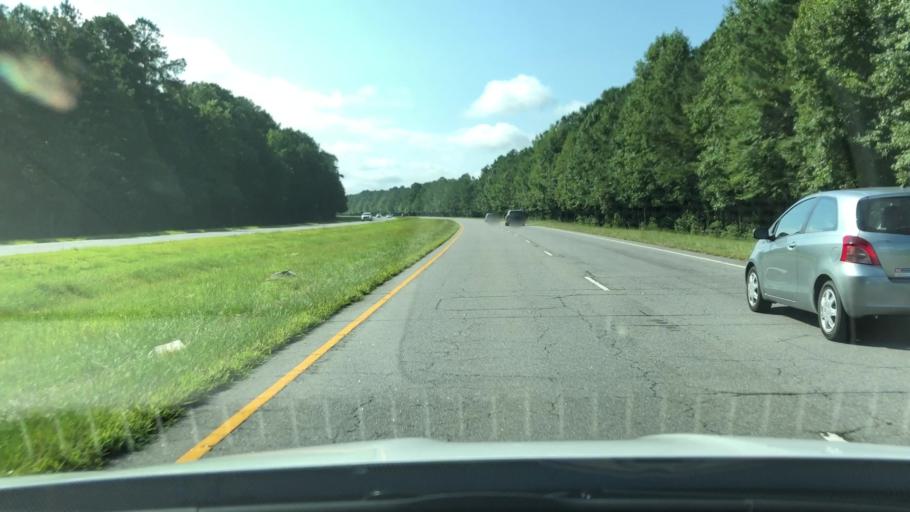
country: US
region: North Carolina
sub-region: Pasquotank County
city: Elizabeth City
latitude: 36.4082
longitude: -76.3388
